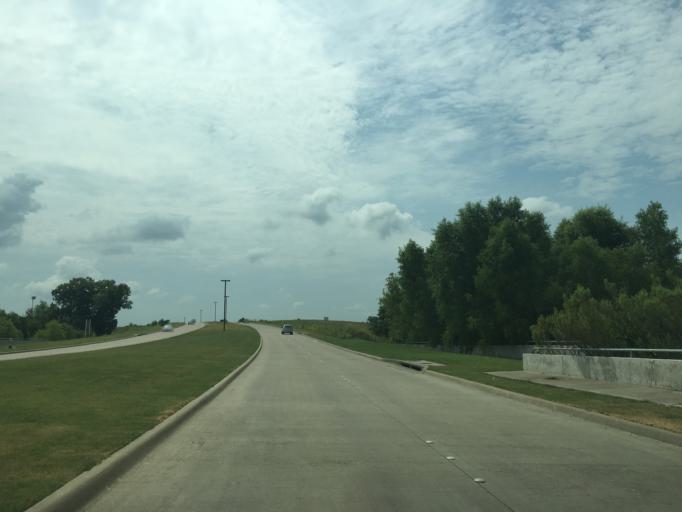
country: US
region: Texas
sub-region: Rockwall County
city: Rockwall
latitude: 32.9773
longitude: -96.4592
